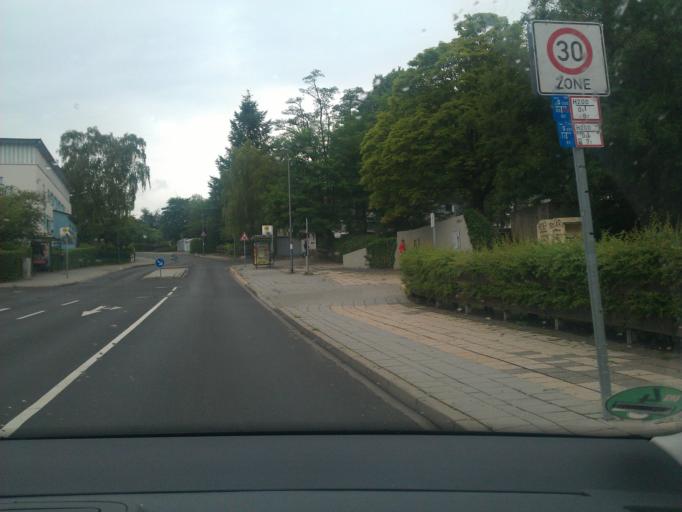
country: DE
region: North Rhine-Westphalia
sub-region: Regierungsbezirk Koln
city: Aachen
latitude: 50.7661
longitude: 6.0608
